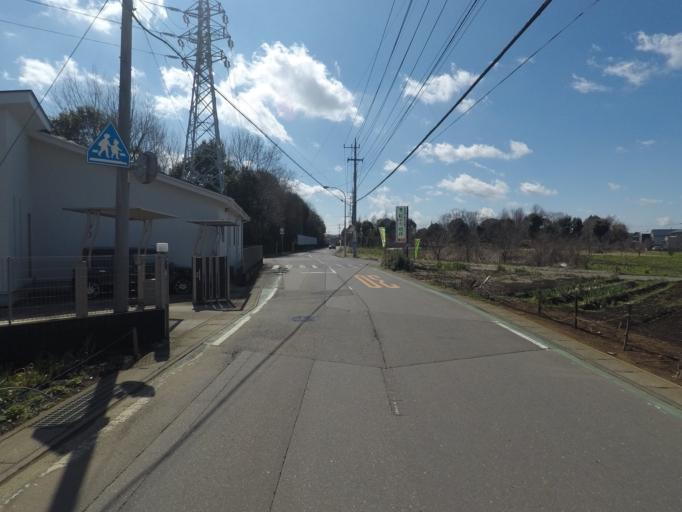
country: JP
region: Ibaraki
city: Naka
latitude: 36.0522
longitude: 140.1140
